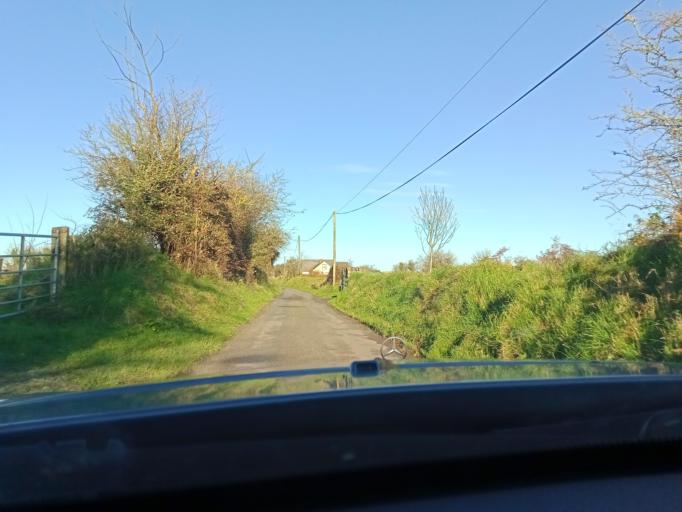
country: IE
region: Leinster
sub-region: Kilkenny
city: Mooncoin
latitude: 52.2950
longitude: -7.2081
